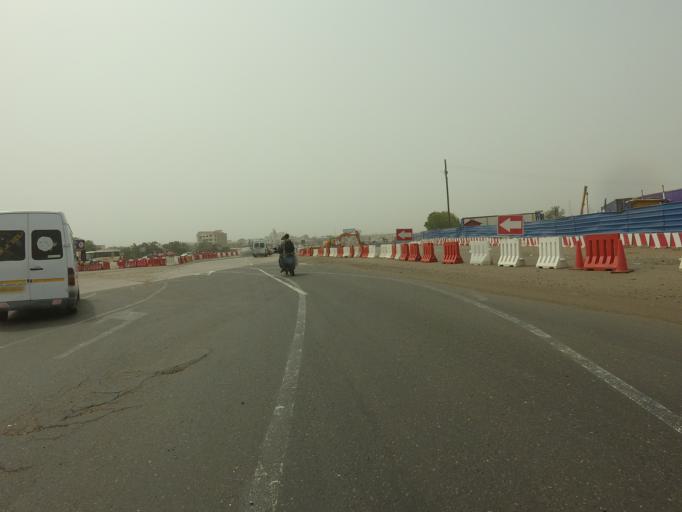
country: GH
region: Greater Accra
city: Tema
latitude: 5.6858
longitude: -0.0181
